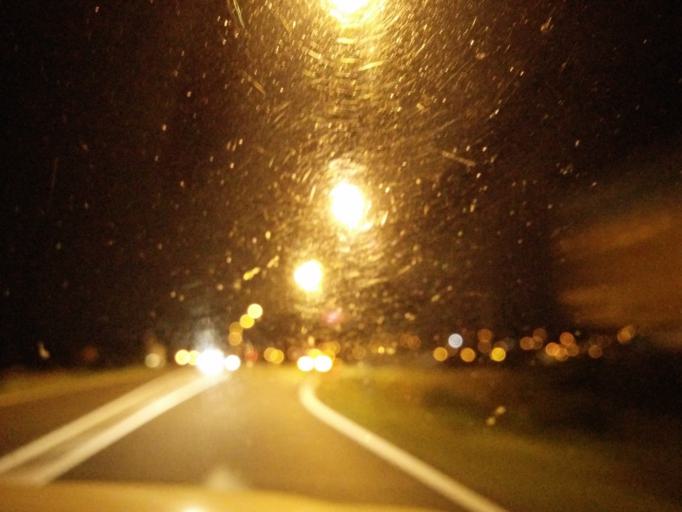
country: HR
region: Brodsko-Posavska
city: Podvinje
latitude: 45.1800
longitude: 18.0305
